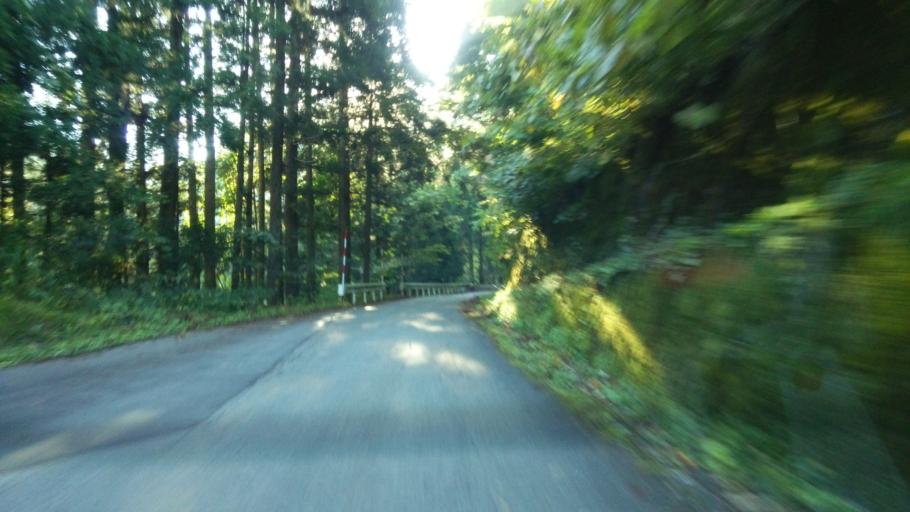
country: JP
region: Fukushima
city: Kitakata
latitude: 37.4004
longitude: 139.7340
